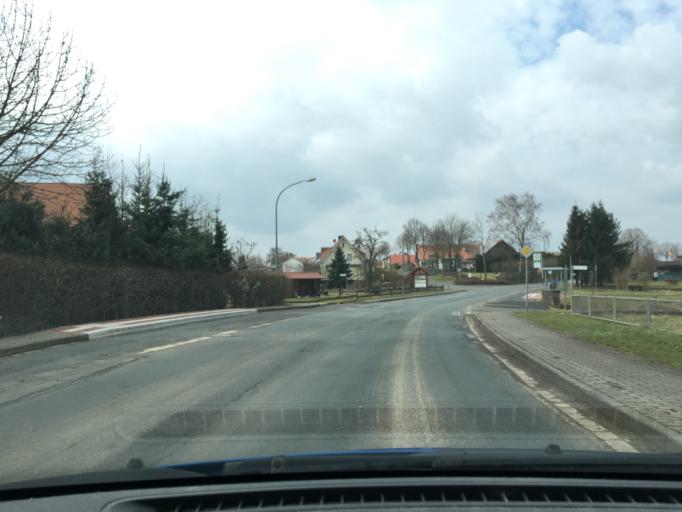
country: DE
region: Lower Saxony
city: Dransfeld
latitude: 51.5390
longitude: 9.7396
